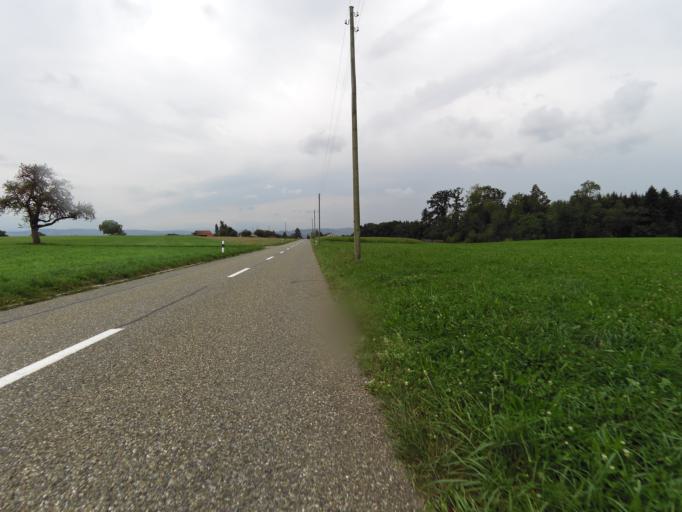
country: CH
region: Thurgau
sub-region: Weinfelden District
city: Wigoltingen
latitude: 47.6272
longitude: 9.0396
